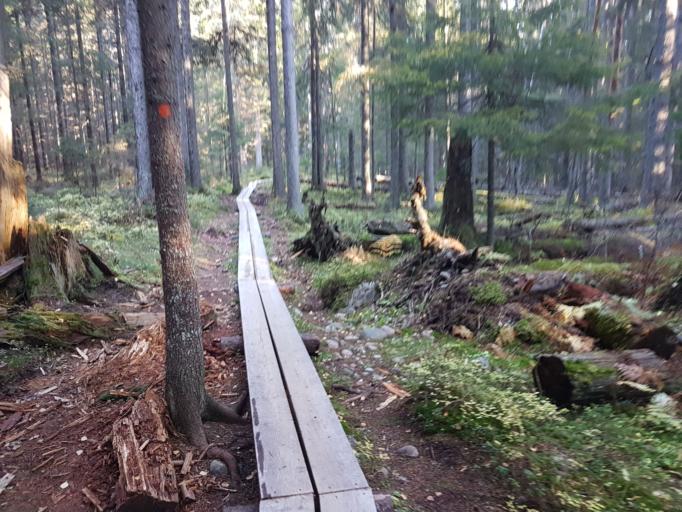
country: SE
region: Vaesternorrland
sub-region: OErnskoeldsviks Kommun
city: Kopmanholmen
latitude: 63.0913
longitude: 18.4978
